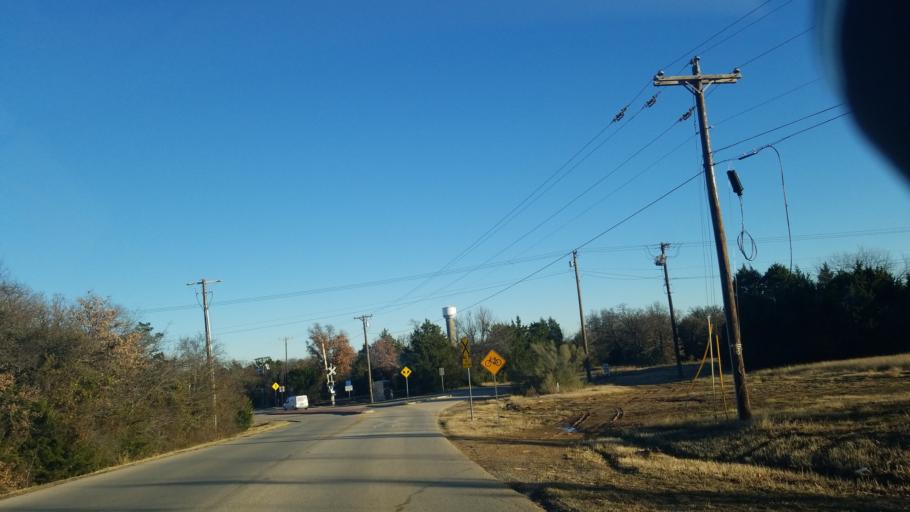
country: US
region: Texas
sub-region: Denton County
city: Corinth
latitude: 33.1635
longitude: -97.0694
